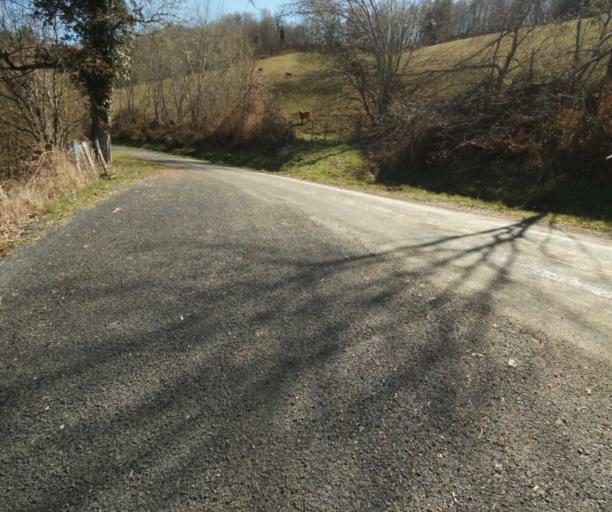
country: FR
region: Limousin
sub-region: Departement de la Correze
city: Chamboulive
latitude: 45.4491
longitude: 1.6811
